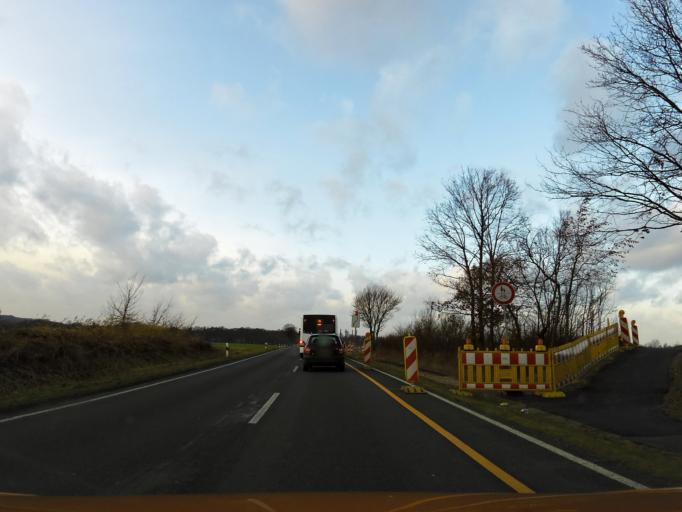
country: DE
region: Lower Saxony
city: Wolfsburg
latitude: 52.4106
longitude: 10.8235
